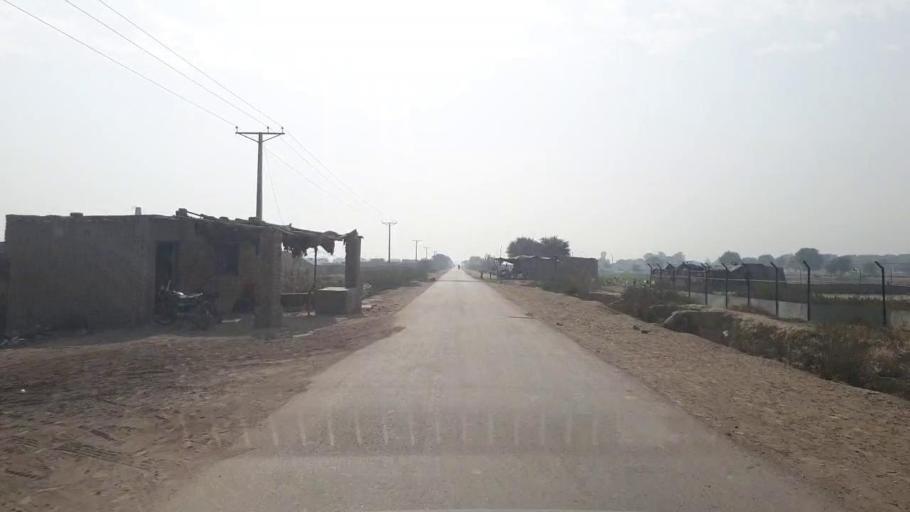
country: PK
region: Sindh
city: Hala
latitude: 25.7755
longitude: 68.4446
